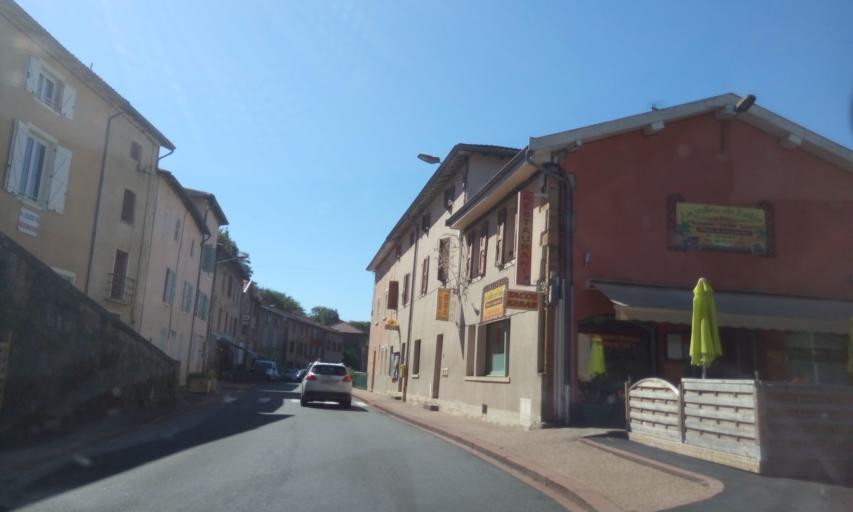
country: FR
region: Rhone-Alpes
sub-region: Departement du Rhone
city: Grandris
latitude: 45.9836
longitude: 4.5090
